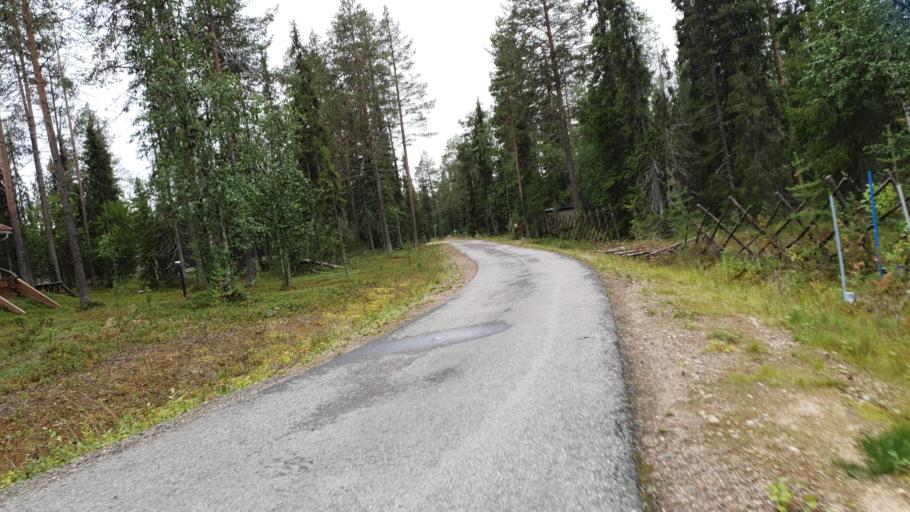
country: FI
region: Lapland
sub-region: Tunturi-Lappi
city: Kolari
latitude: 67.5999
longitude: 24.1816
